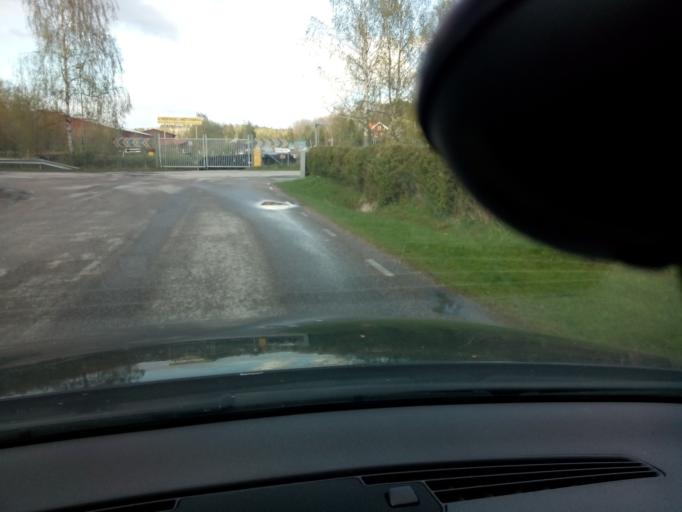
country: SE
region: Soedermanland
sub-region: Nykopings Kommun
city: Nykoping
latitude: 58.7812
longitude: 17.0973
